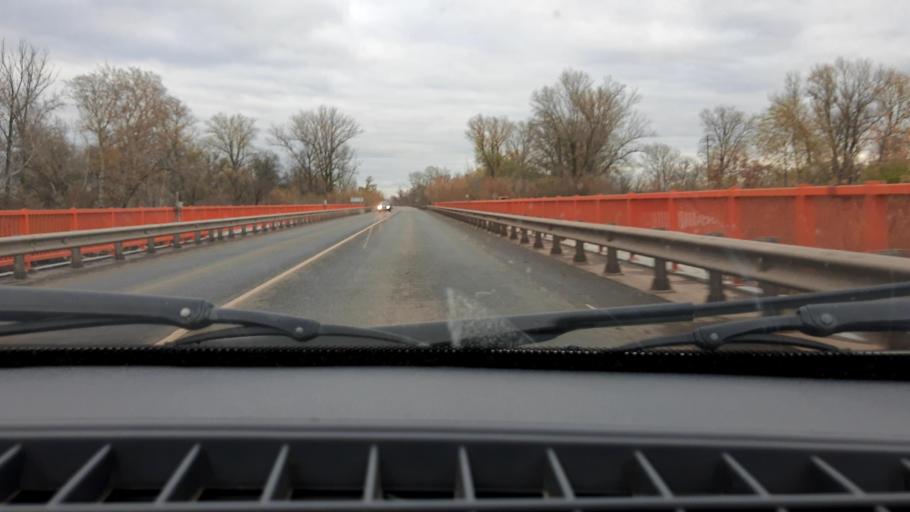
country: RU
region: Bashkortostan
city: Ufa
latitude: 54.5695
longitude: 55.9750
